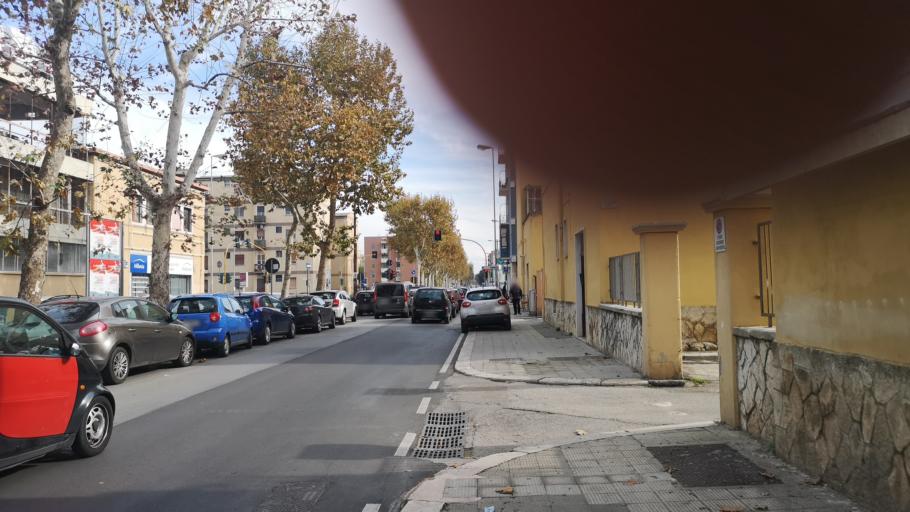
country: IT
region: Apulia
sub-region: Provincia di Bari
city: Bari
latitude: 41.1154
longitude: 16.8866
